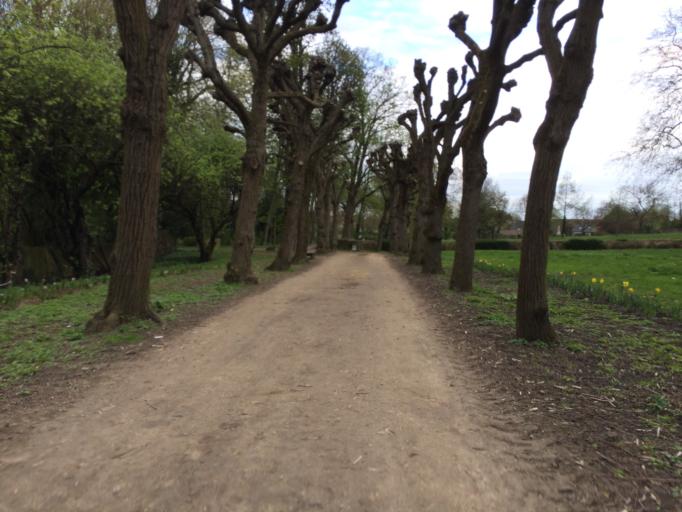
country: FR
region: Ile-de-France
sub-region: Departement de l'Essonne
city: Wissous
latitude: 48.7343
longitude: 2.3295
